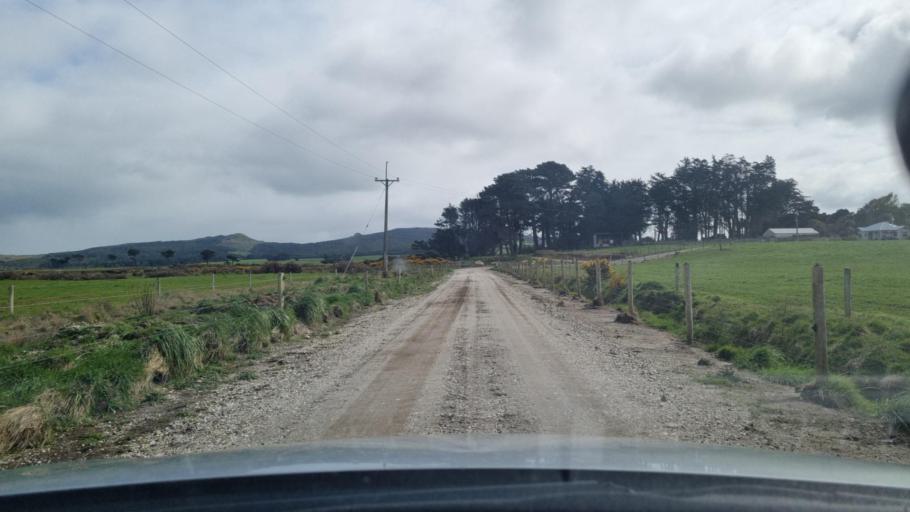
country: NZ
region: Southland
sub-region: Invercargill City
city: Bluff
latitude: -46.5258
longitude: 168.3003
